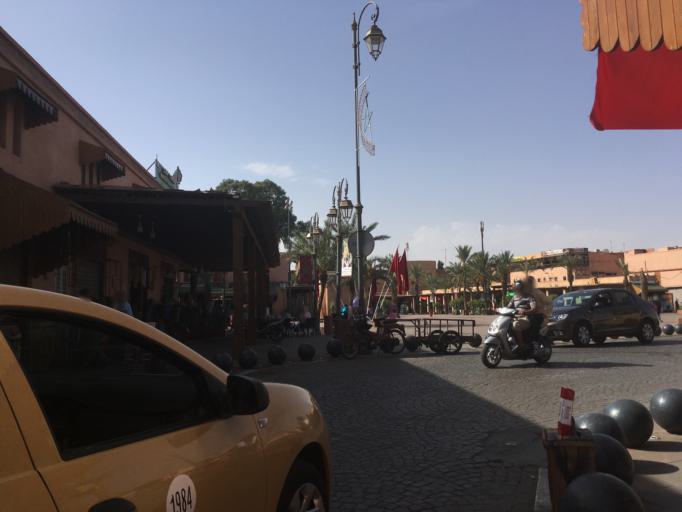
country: MA
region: Marrakech-Tensift-Al Haouz
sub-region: Marrakech
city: Marrakesh
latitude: 31.6205
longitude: -7.9847
